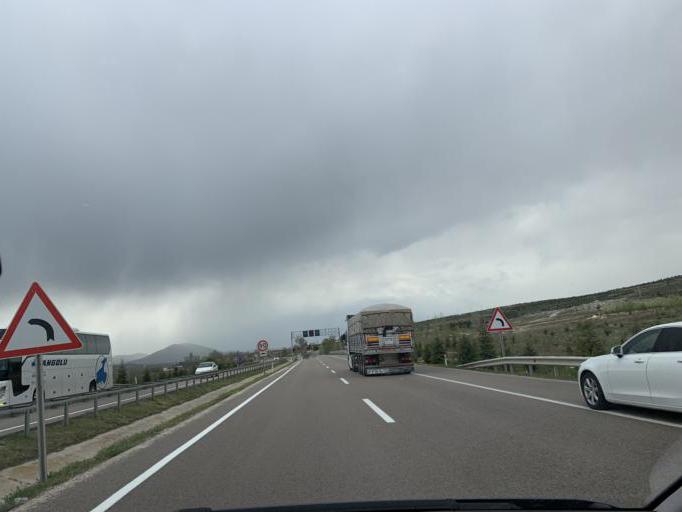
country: TR
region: Eskisehir
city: Sivrihisar
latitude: 39.5344
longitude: 31.6428
